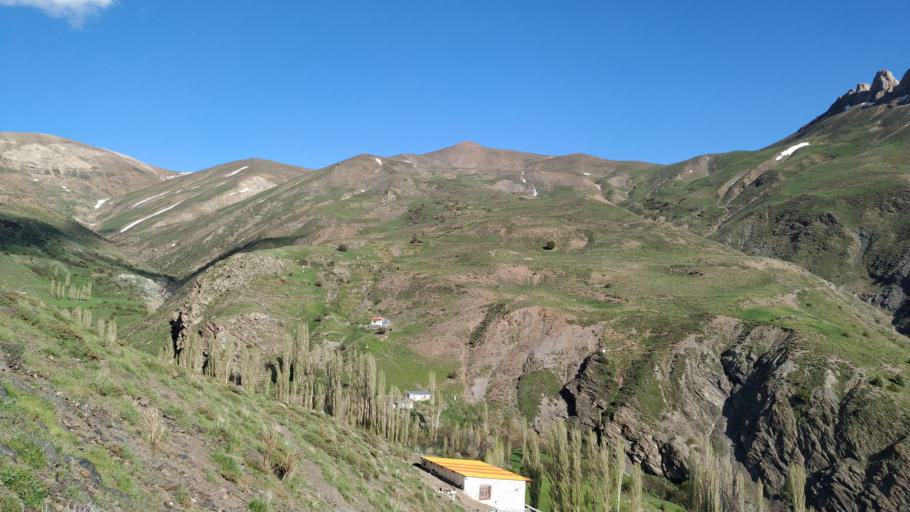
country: IR
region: Zanjan
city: Ab Bar
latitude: 37.1172
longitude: 48.9224
